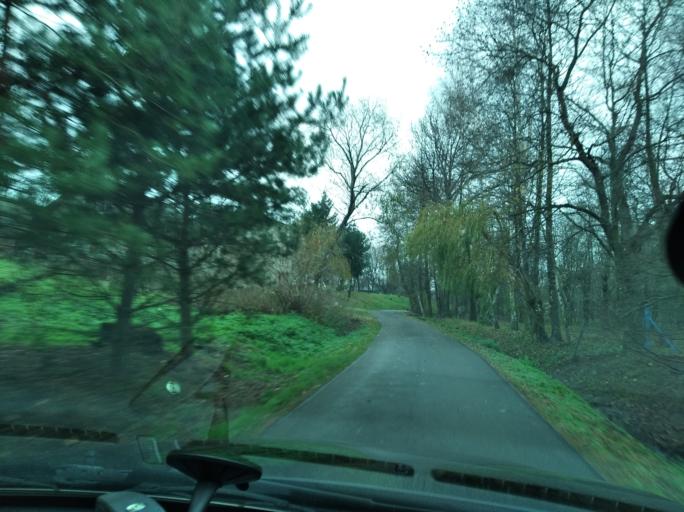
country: PL
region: Subcarpathian Voivodeship
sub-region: Powiat przeworski
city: Sietesz
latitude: 50.0022
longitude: 22.3524
